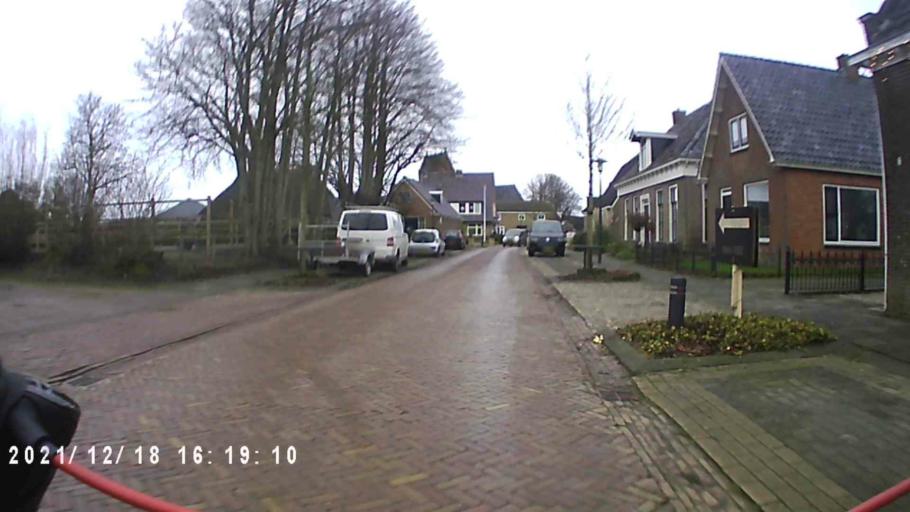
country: NL
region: Friesland
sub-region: Gemeente Dongeradeel
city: Anjum
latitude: 53.3777
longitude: 6.0548
